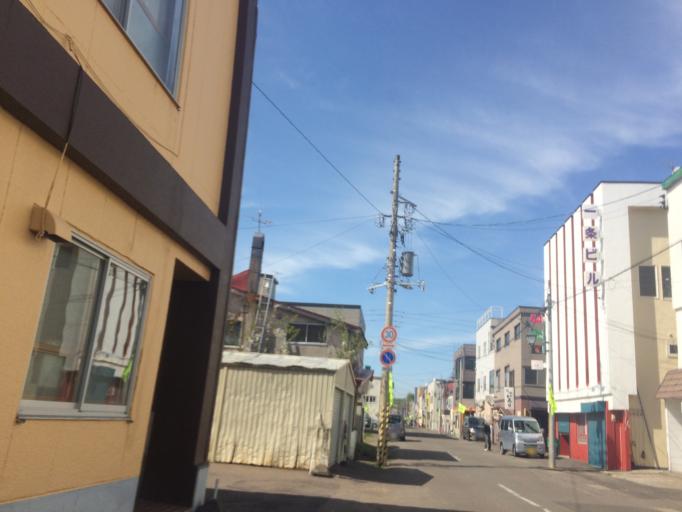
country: JP
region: Hokkaido
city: Niseko Town
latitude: 42.9017
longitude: 140.7512
